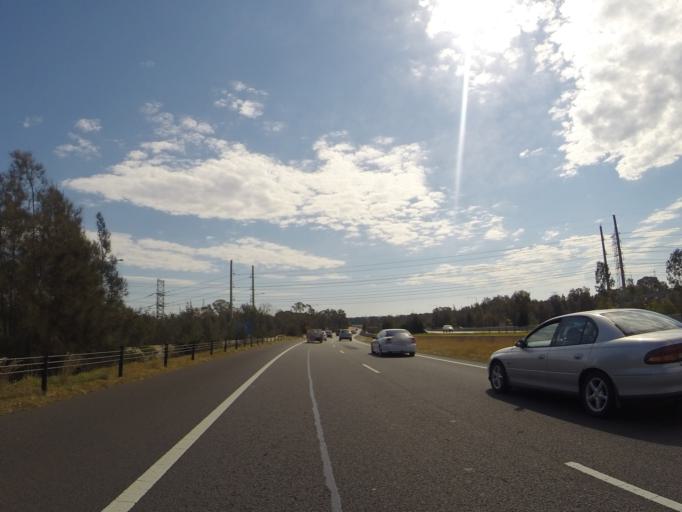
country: AU
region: New South Wales
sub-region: Liverpool
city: Miller
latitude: -33.9327
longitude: 150.8682
